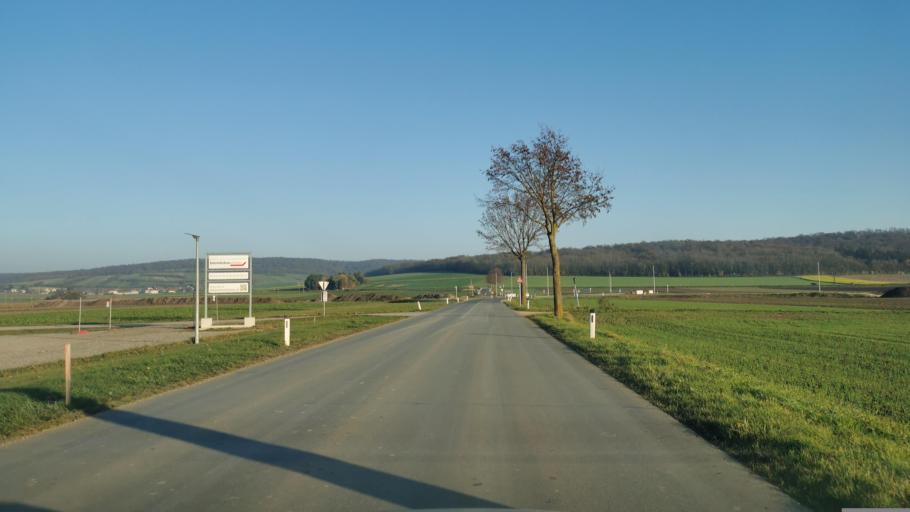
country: AT
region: Lower Austria
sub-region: Politischer Bezirk Korneuburg
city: Harmannsdorf
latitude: 48.3903
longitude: 16.3838
